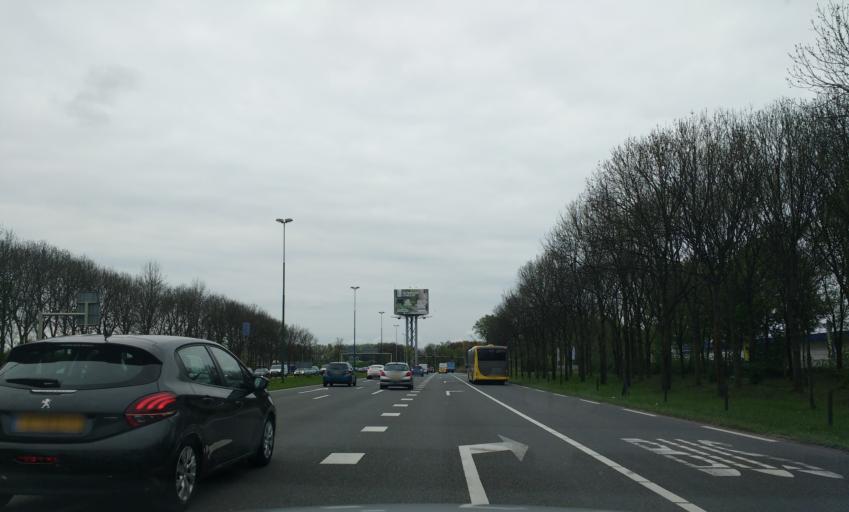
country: NL
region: Utrecht
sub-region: Gemeente Utrecht
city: Lunetten
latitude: 52.0524
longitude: 5.1206
